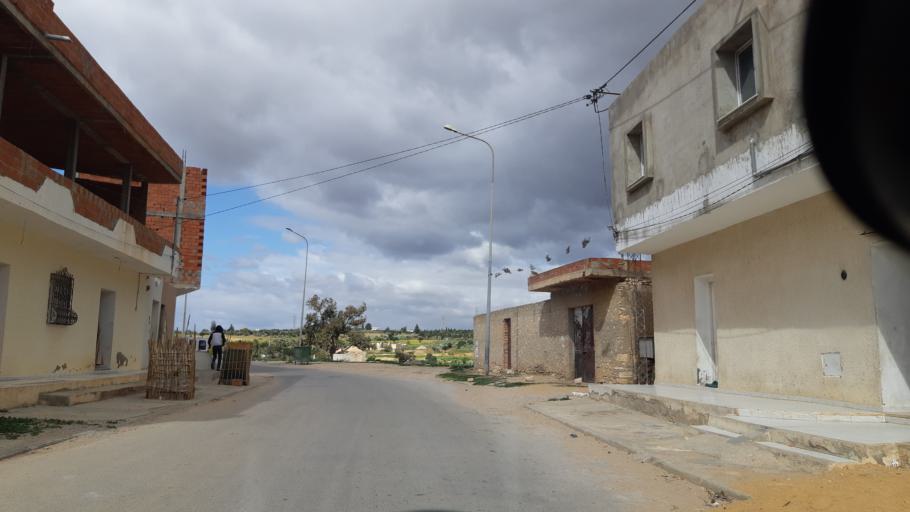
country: TN
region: Susah
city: Akouda
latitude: 35.8732
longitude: 10.5193
